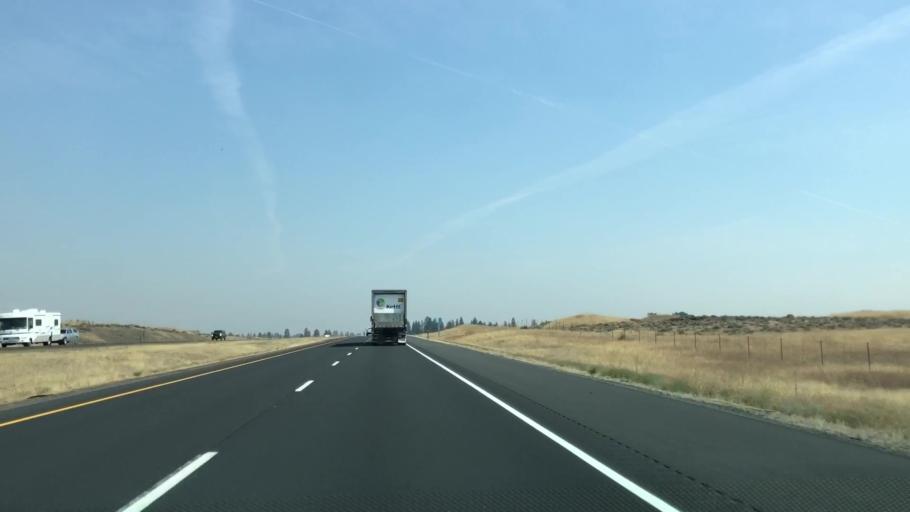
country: US
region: Washington
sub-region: Spokane County
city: Medical Lake
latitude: 47.3839
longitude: -117.8585
